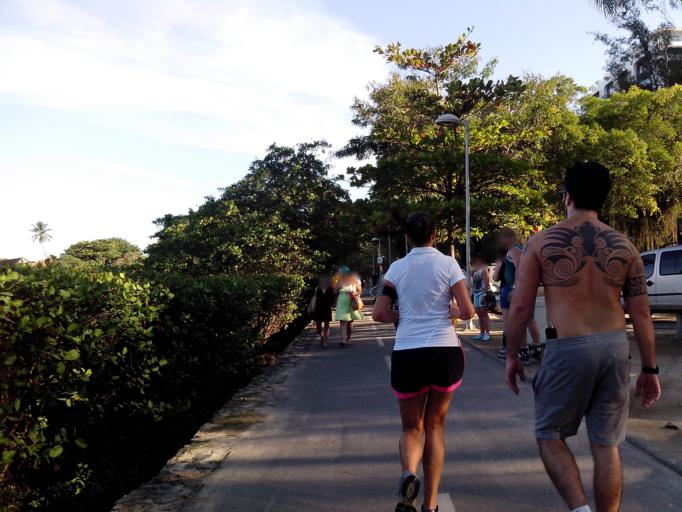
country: BR
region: Rio de Janeiro
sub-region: Rio De Janeiro
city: Rio de Janeiro
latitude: -22.9653
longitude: -43.2157
